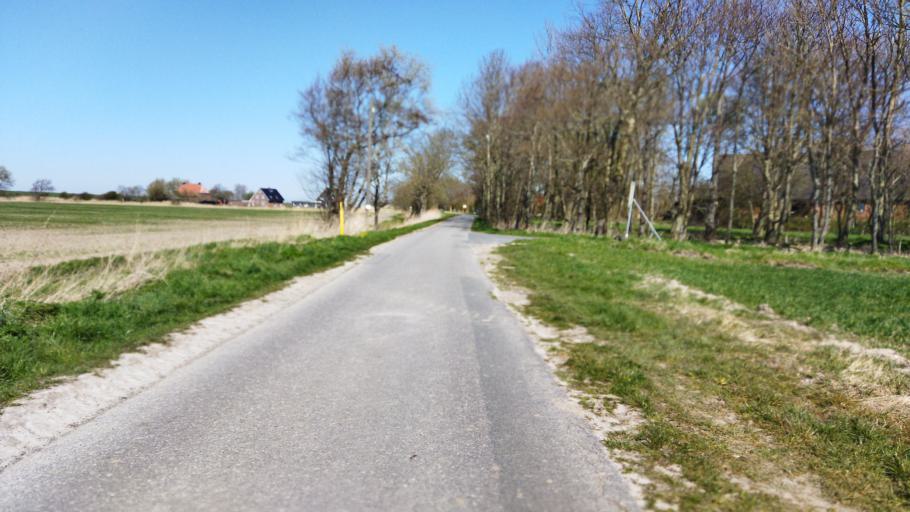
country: DE
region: Lower Saxony
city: Misselwarden
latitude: 53.6921
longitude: 8.4900
